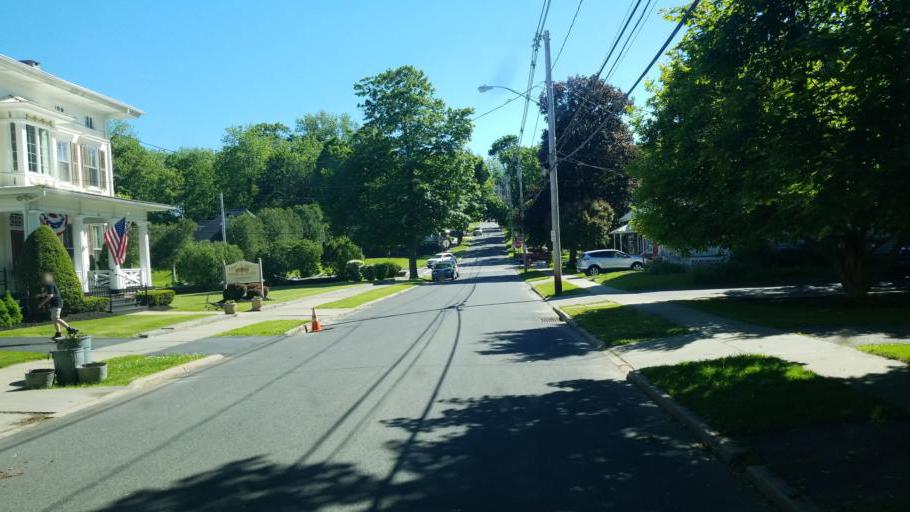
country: US
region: New York
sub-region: Montgomery County
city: Canajoharie
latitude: 42.9032
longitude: -74.5755
